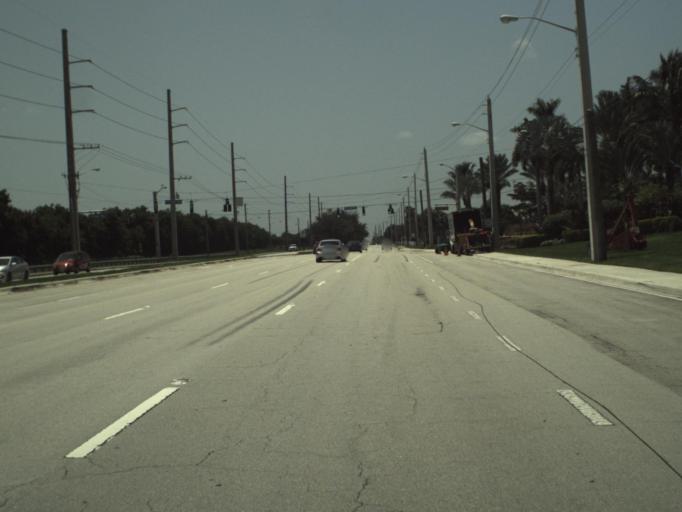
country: US
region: Florida
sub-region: Palm Beach County
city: Villages of Oriole
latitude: 26.5031
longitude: -80.1475
